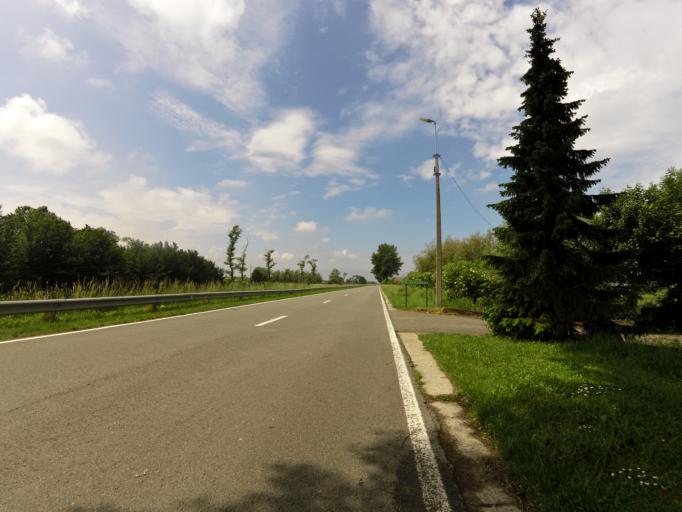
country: BE
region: Flanders
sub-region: Provincie West-Vlaanderen
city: Nieuwpoort
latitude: 51.1305
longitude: 2.7974
